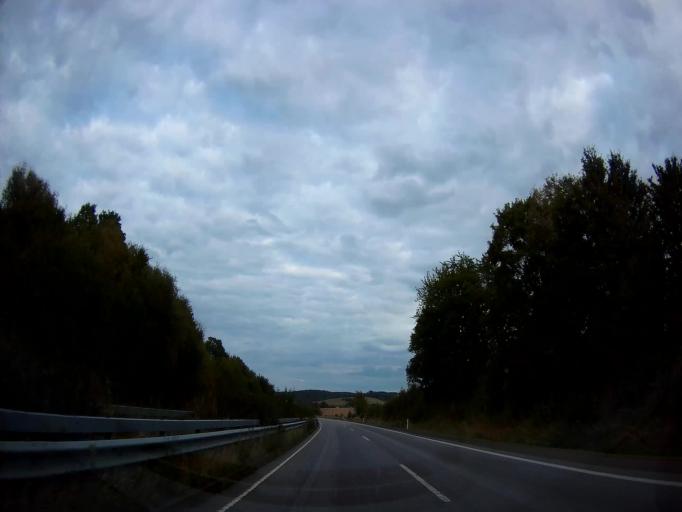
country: DE
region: Rheinland-Pfalz
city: Albessen
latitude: 49.5184
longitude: 7.3396
